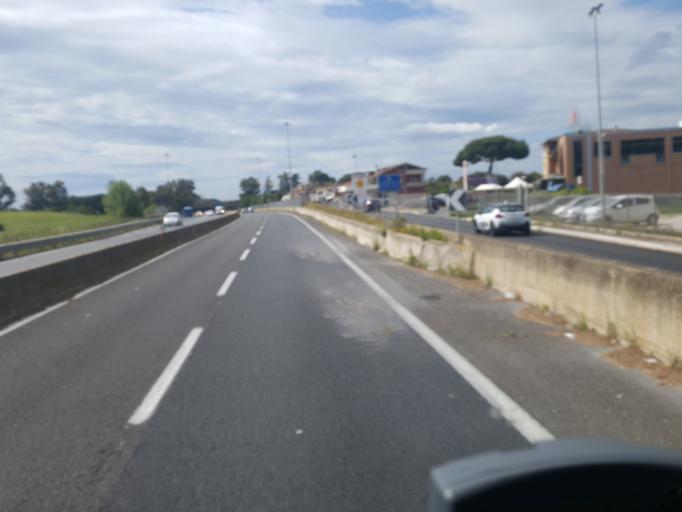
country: IT
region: Latium
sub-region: Citta metropolitana di Roma Capitale
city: Ara Nova
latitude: 41.9164
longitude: 12.2420
